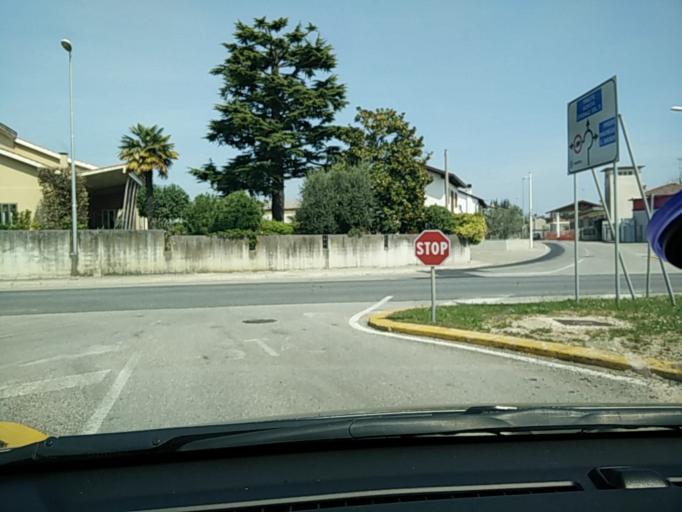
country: IT
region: Friuli Venezia Giulia
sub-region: Provincia di Udine
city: Manzano
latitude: 45.9873
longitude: 13.3704
